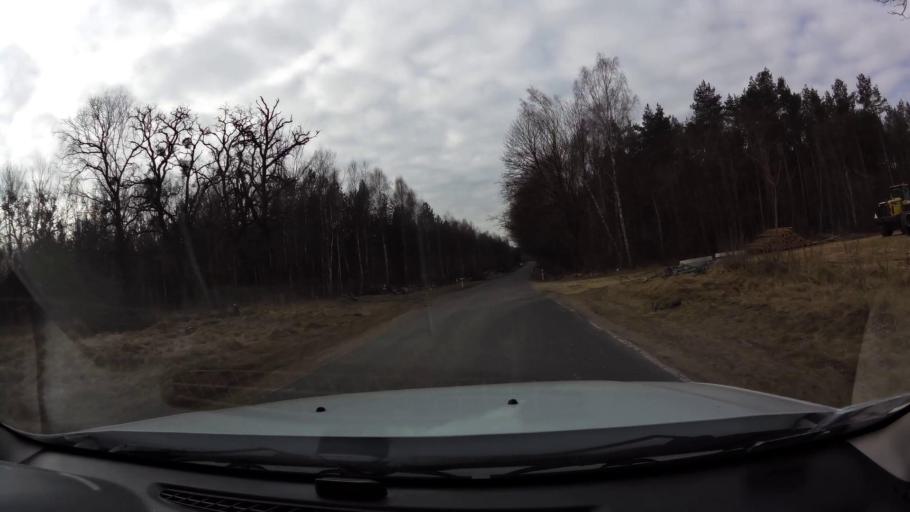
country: PL
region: West Pomeranian Voivodeship
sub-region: Powiat mysliborski
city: Debno
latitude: 52.7174
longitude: 14.6779
